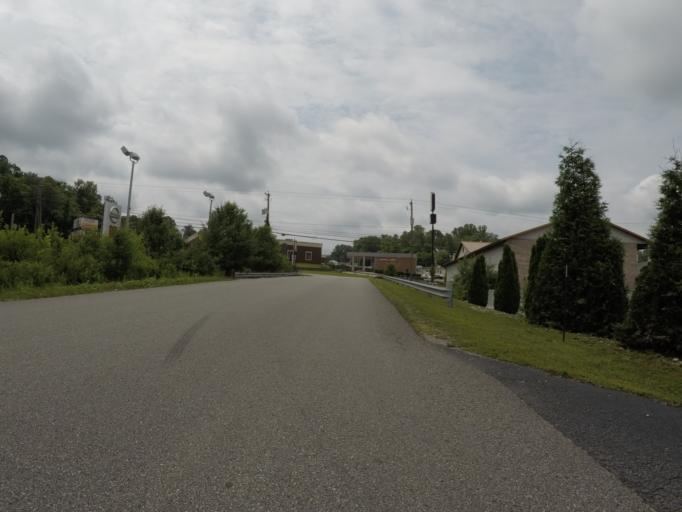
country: US
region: West Virginia
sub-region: Cabell County
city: Pea Ridge
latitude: 38.4132
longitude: -82.3421
